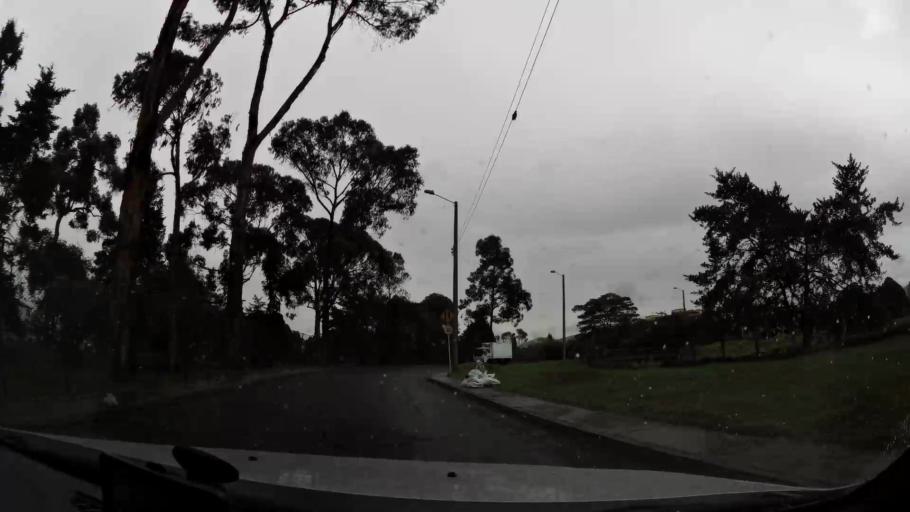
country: CO
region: Bogota D.C.
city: Bogota
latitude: 4.6626
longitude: -74.1225
